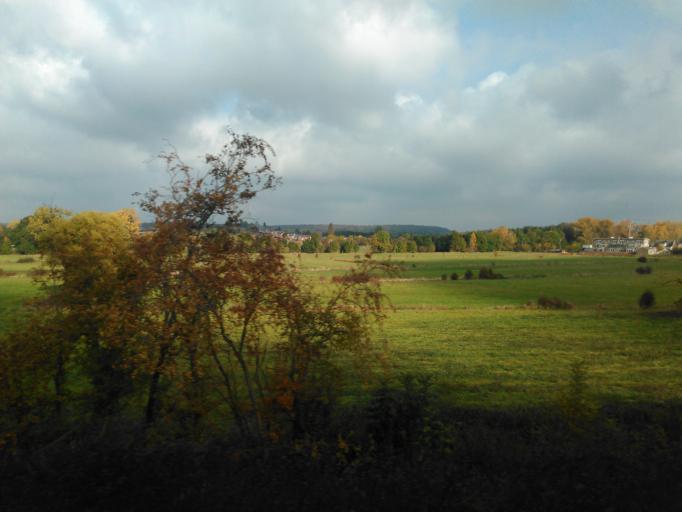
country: LU
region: Luxembourg
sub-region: Canton d'Esch-sur-Alzette
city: Bettembourg
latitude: 49.5155
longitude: 6.0892
